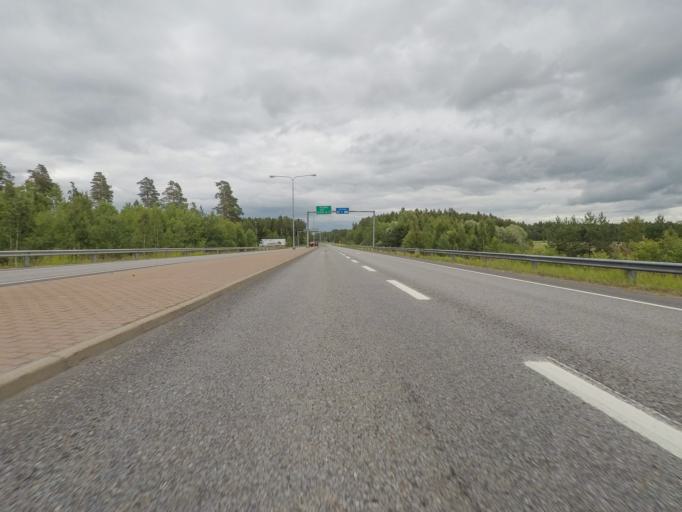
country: FI
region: Varsinais-Suomi
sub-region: Turku
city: Piikkioe
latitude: 60.4428
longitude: 22.4932
